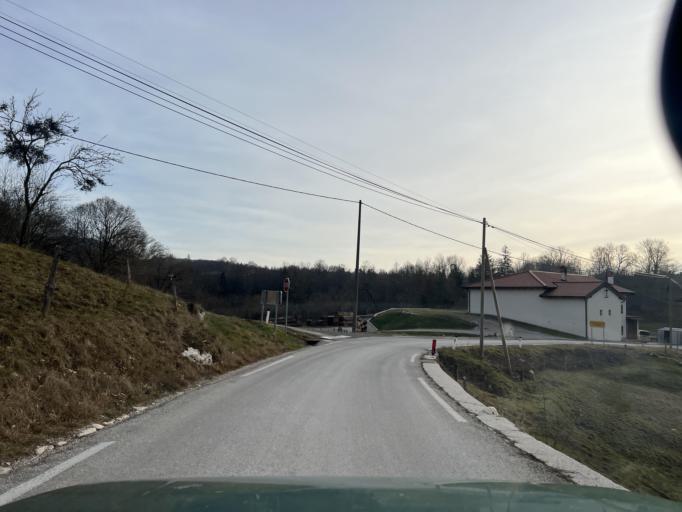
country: SI
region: Nova Gorica
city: Sempas
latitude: 45.9754
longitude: 13.7444
